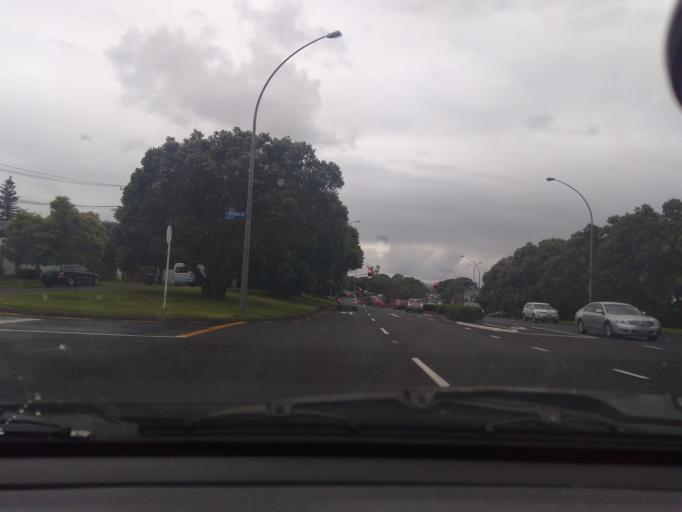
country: NZ
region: Auckland
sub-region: Auckland
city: Auckland
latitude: -36.8778
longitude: 174.7271
